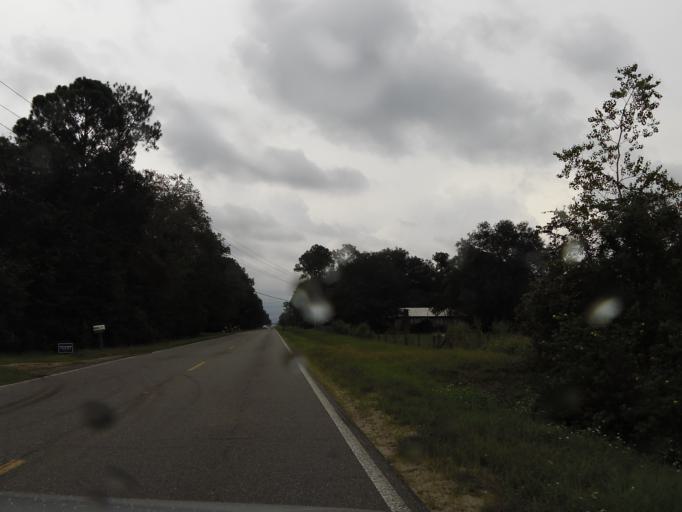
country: US
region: Florida
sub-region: Clay County
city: Middleburg
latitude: 30.1142
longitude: -81.8546
